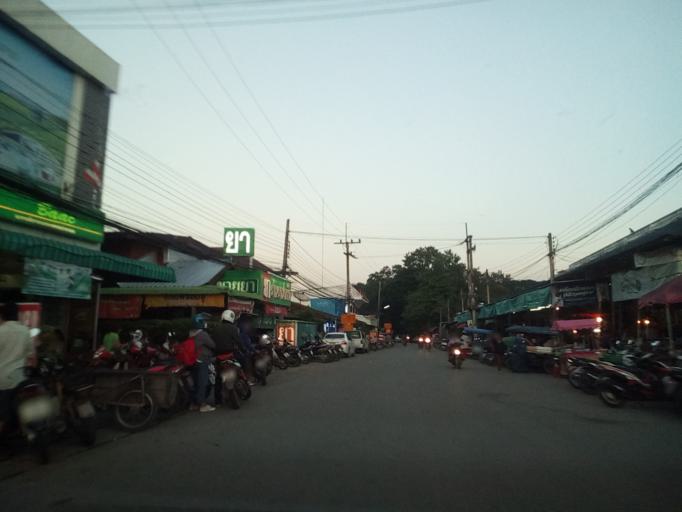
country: TH
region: Chiang Mai
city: Saraphi
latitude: 18.6489
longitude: 99.0426
